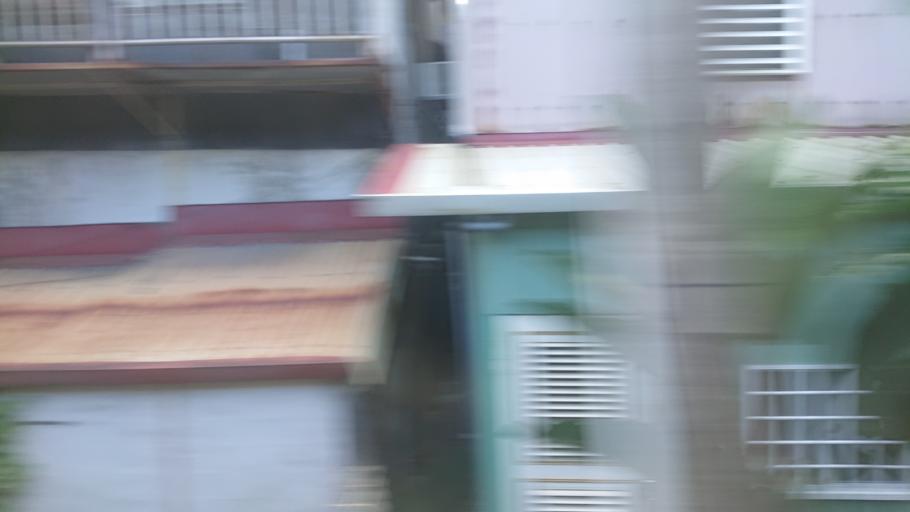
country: TW
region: Taiwan
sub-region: Hualien
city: Hualian
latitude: 23.9857
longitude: 121.5973
